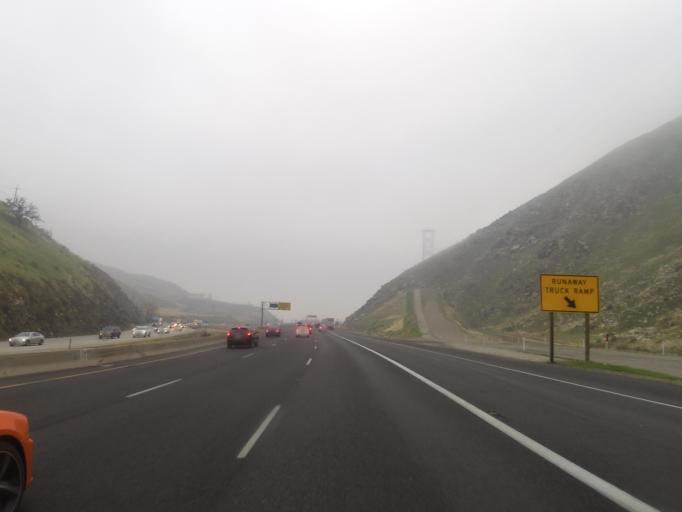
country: US
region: California
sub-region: Kern County
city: Lebec
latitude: 34.9130
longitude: -118.9233
